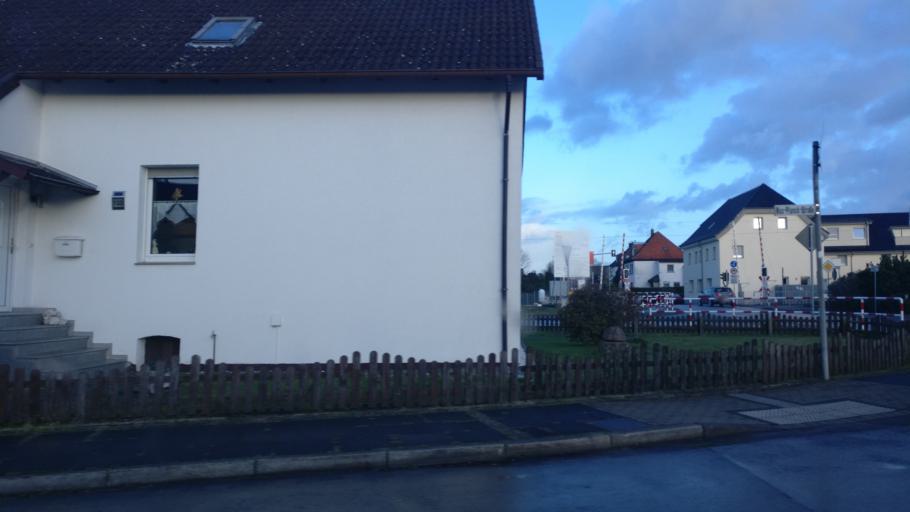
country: DE
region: North Rhine-Westphalia
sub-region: Regierungsbezirk Detmold
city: Lage
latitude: 52.0261
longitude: 8.7647
